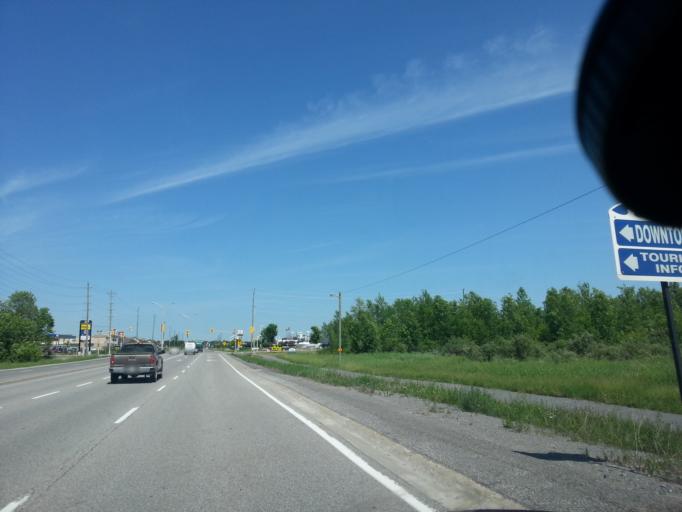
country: CA
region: Ontario
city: Carleton Place
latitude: 45.1386
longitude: -76.1254
